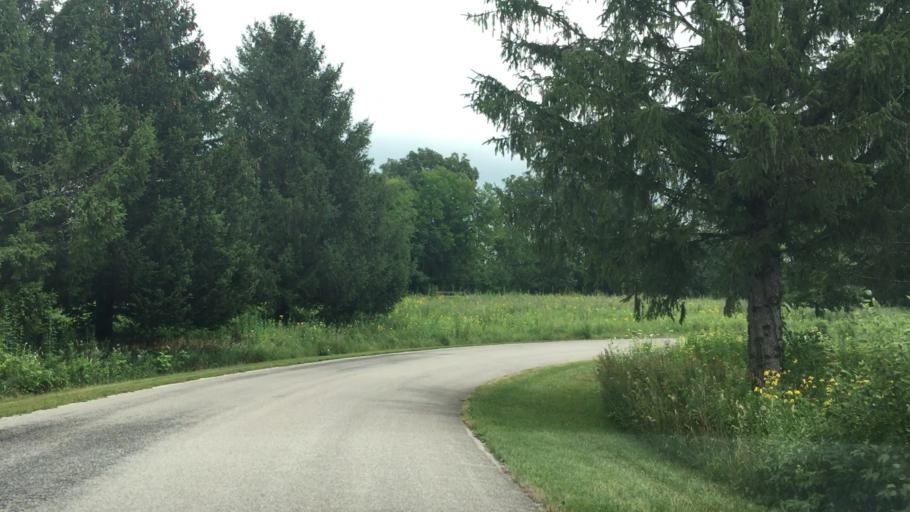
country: US
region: Iowa
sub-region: Johnson County
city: Tiffin
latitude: 41.7381
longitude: -91.7286
